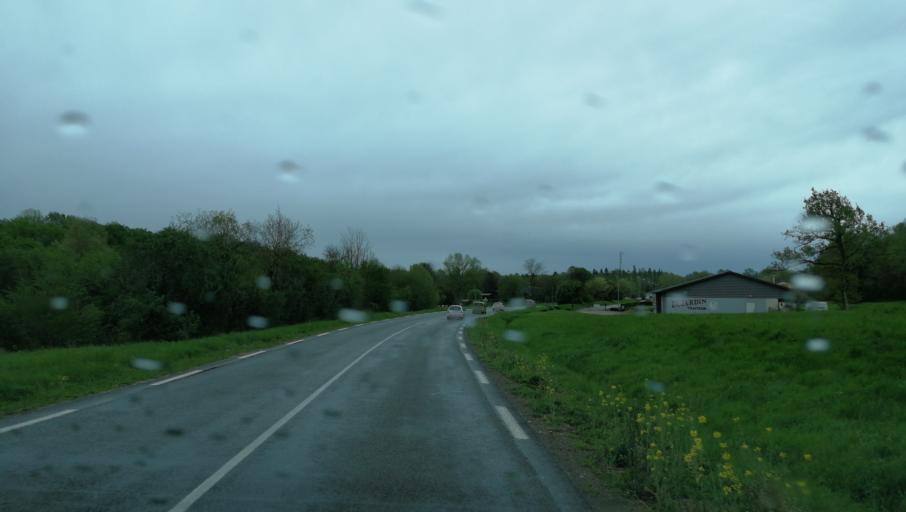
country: FR
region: Franche-Comte
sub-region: Departement du Jura
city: Bletterans
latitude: 46.7138
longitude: 5.4770
